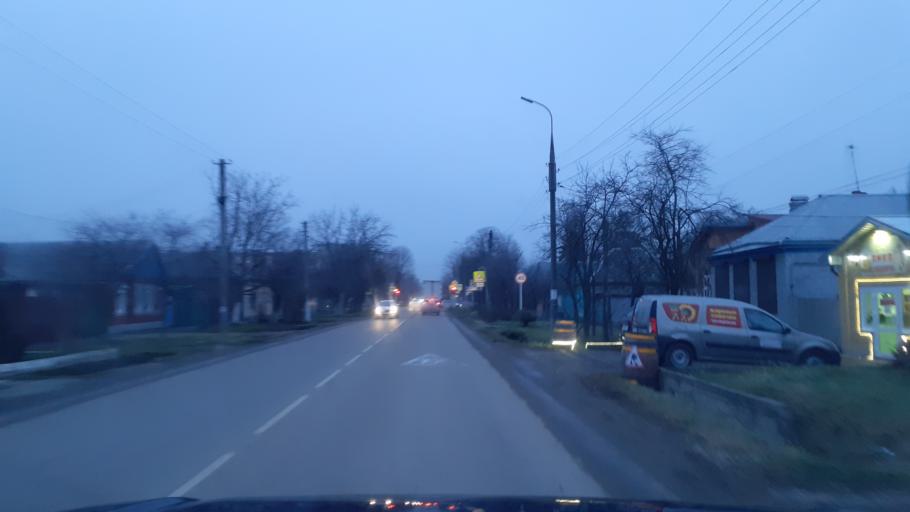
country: RU
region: Adygeya
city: Maykop
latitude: 44.6150
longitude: 40.0944
